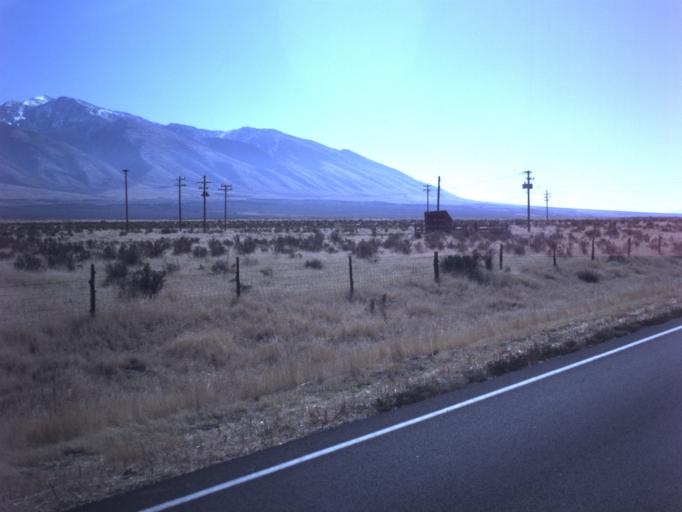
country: US
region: Utah
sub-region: Tooele County
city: Grantsville
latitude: 40.5246
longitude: -112.7477
